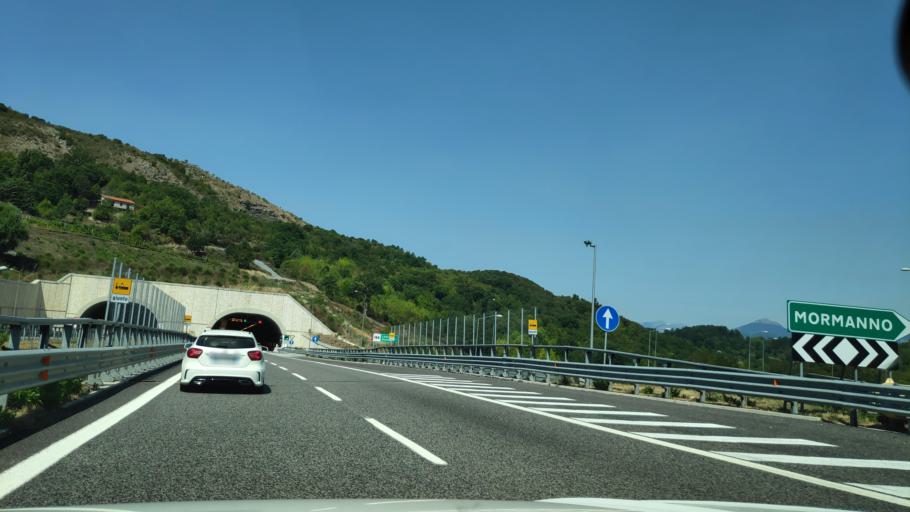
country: IT
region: Calabria
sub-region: Provincia di Cosenza
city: Mormanno
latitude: 39.9000
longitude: 15.9752
